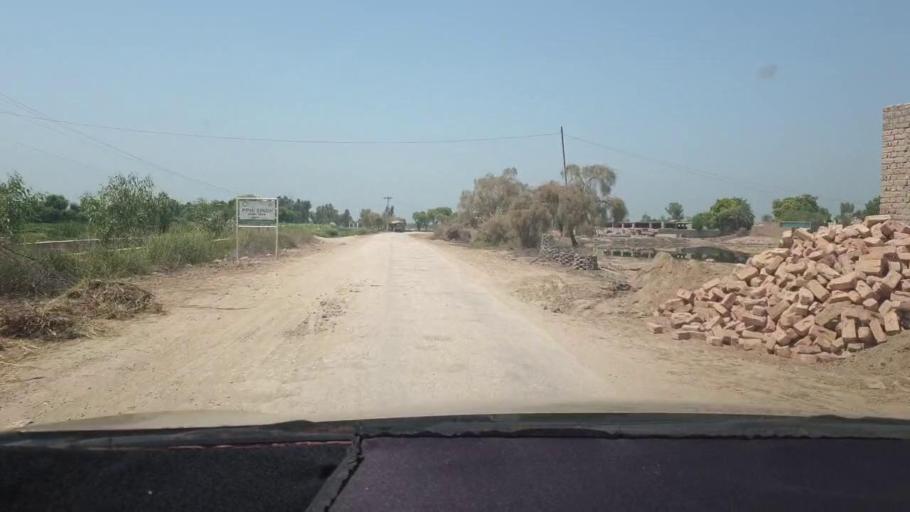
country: PK
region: Sindh
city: Miro Khan
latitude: 27.6697
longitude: 68.0615
